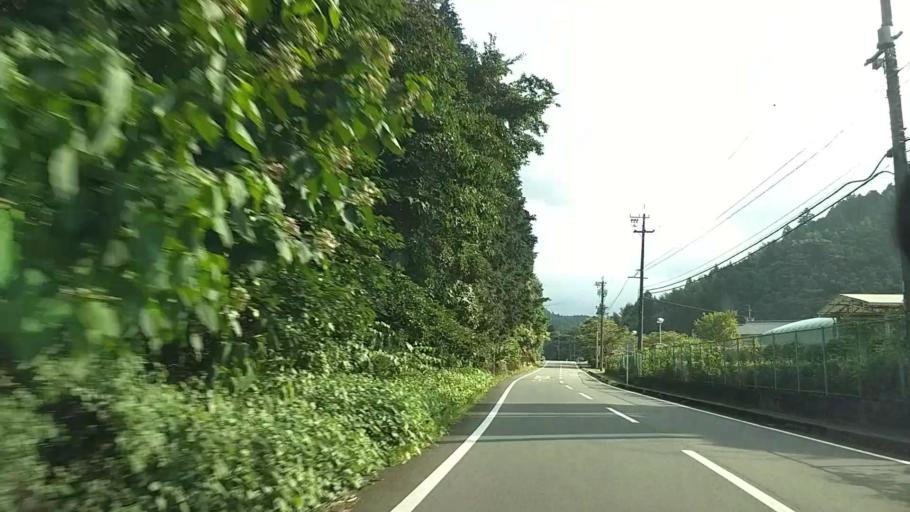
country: JP
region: Shizuoka
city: Fujinomiya
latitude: 35.1860
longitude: 138.5471
